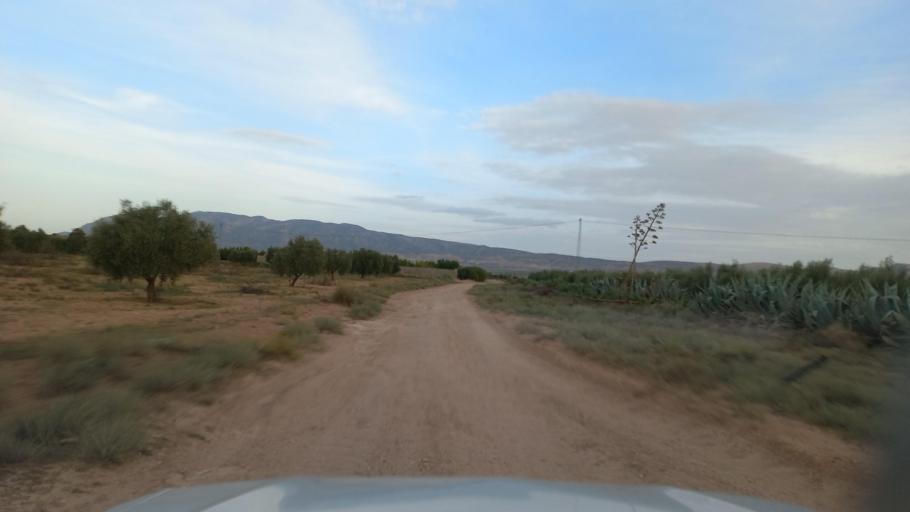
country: TN
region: Al Qasrayn
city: Sbiba
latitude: 35.4227
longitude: 9.1041
